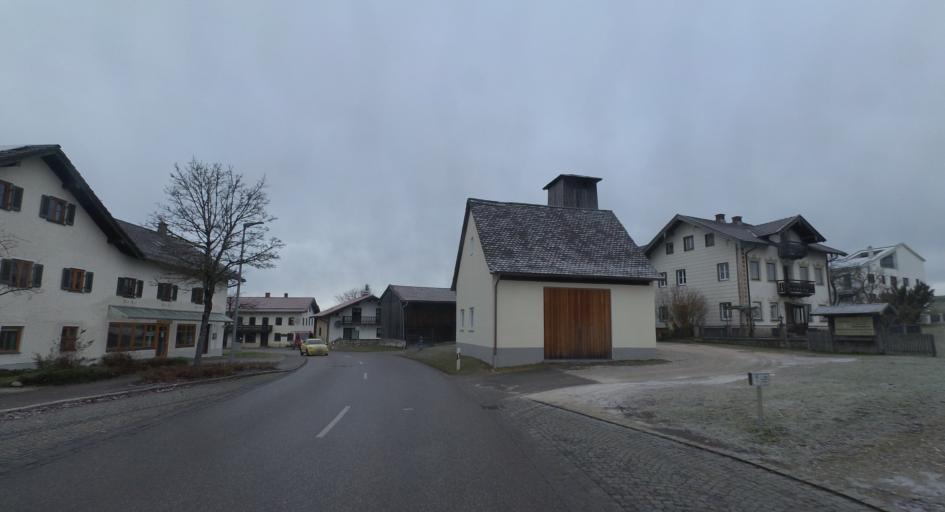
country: DE
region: Bavaria
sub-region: Upper Bavaria
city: Traunstein
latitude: 47.9245
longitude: 12.6527
